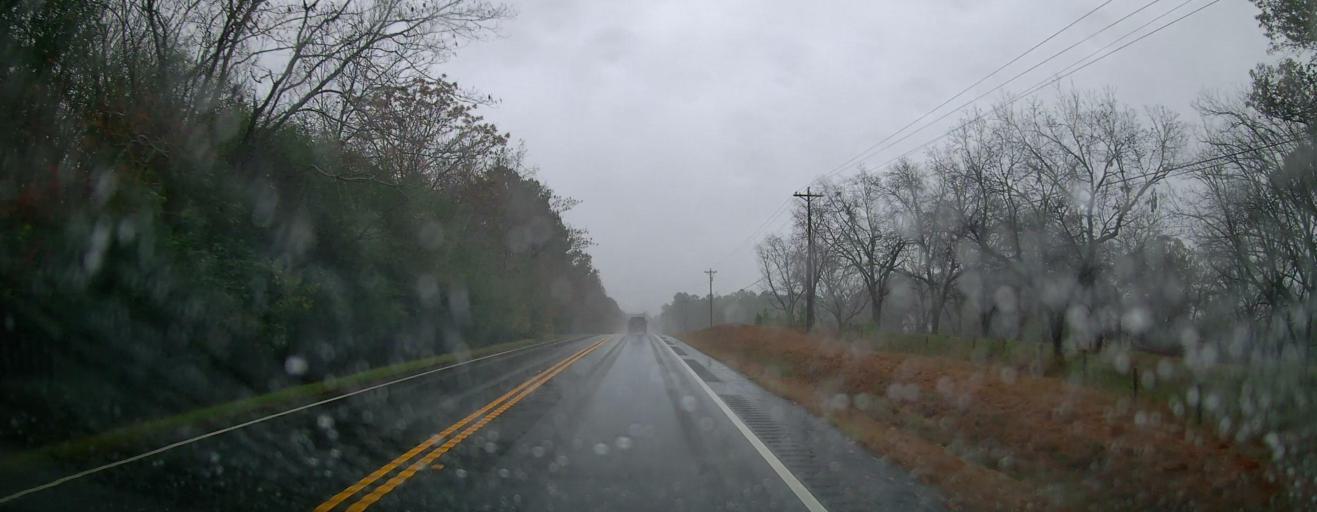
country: US
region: Georgia
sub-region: Putnam County
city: Eatonton
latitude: 33.2049
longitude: -83.4345
